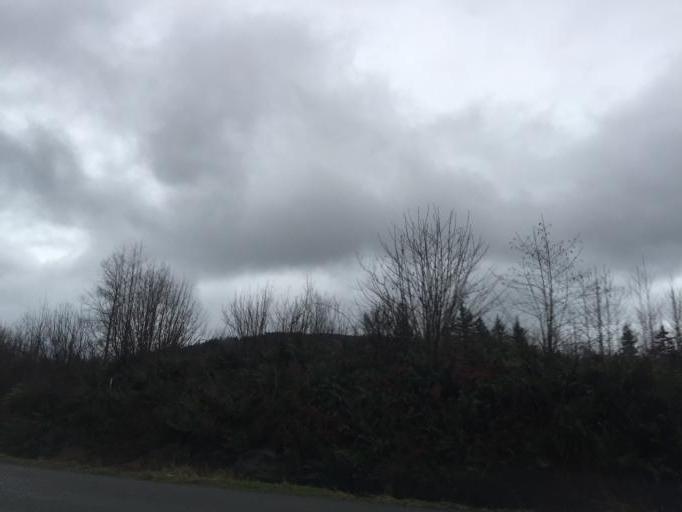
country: US
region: Washington
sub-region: King County
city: Fall City
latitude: 47.5120
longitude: -121.8844
